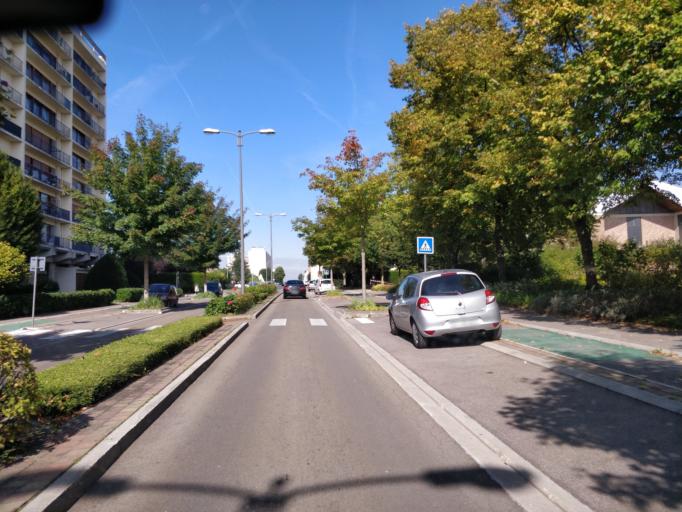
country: FR
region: Champagne-Ardenne
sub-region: Departement de l'Aube
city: Rosieres-pres-Troyes
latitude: 48.2783
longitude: 4.0751
